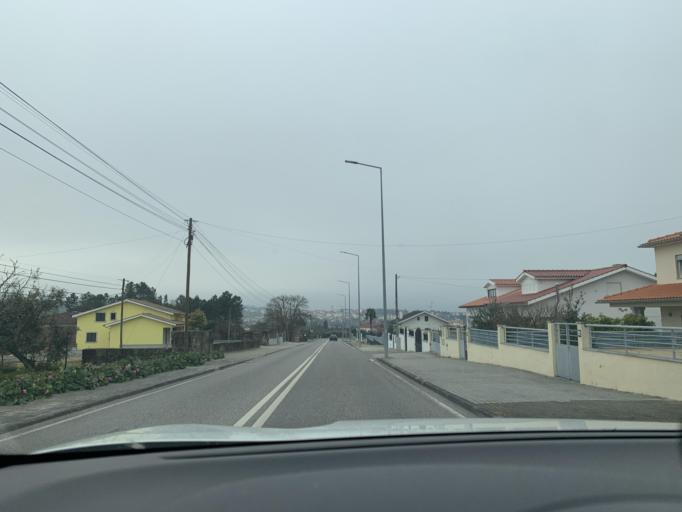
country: PT
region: Viseu
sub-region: Concelho de Tondela
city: Tondela
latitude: 40.5268
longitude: -8.0618
